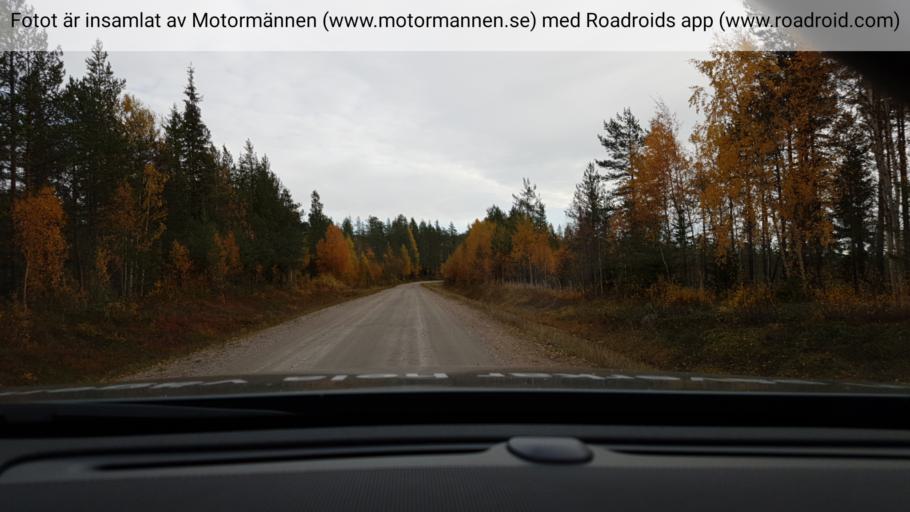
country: SE
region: Norrbotten
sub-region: Overkalix Kommun
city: OEverkalix
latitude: 66.2883
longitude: 22.9676
